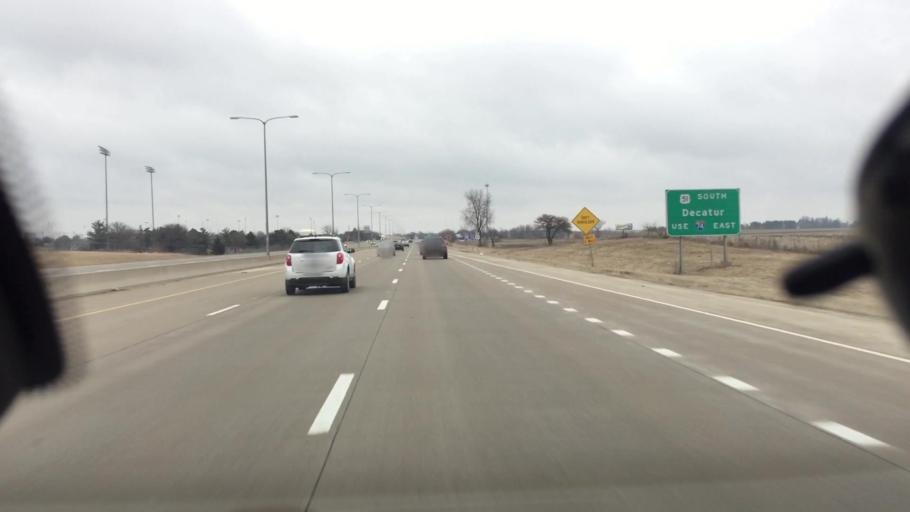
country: US
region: Illinois
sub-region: McLean County
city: Normal
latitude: 40.5260
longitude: -89.0282
